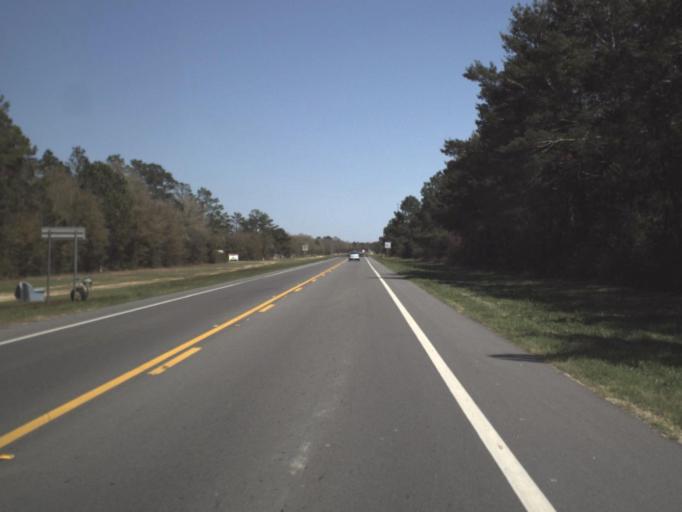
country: US
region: Florida
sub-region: Walton County
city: DeFuniak Springs
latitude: 30.7497
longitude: -86.2574
